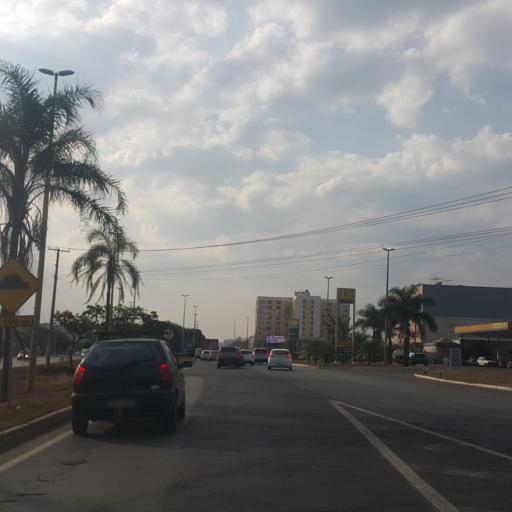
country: BR
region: Federal District
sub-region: Brasilia
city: Brasilia
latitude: -15.8740
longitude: -48.0286
